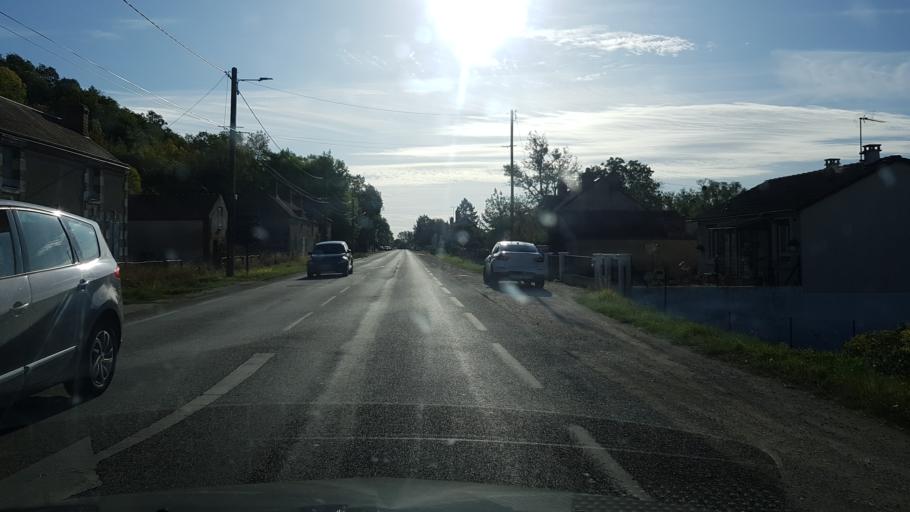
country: FR
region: Centre
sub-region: Departement du Loiret
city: Saint-Martin-sur-Ocre
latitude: 47.6754
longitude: 2.6565
